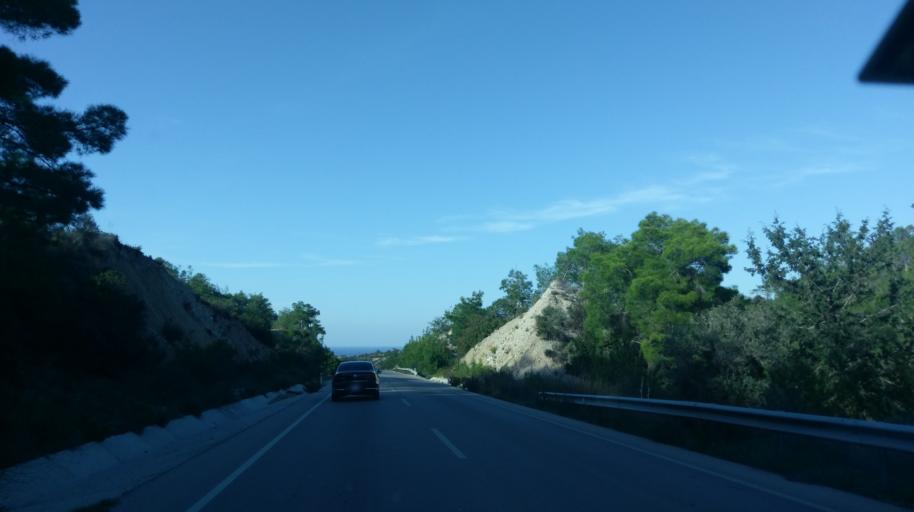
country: CY
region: Ammochostos
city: Lefkonoiko
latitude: 35.3579
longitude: 33.7122
